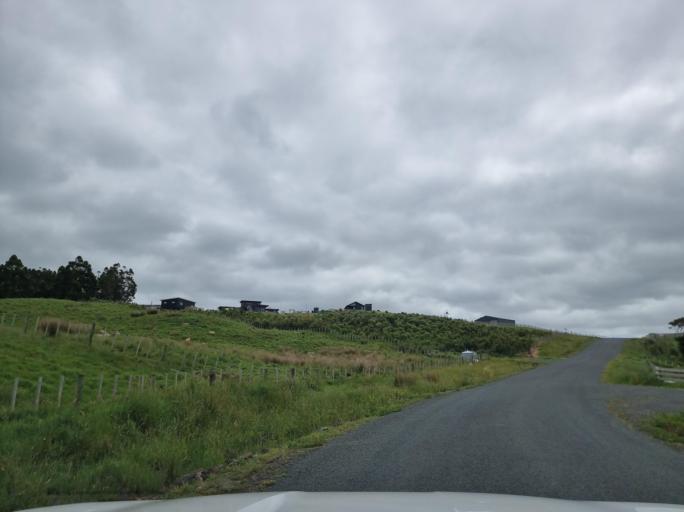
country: NZ
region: Auckland
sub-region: Auckland
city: Wellsford
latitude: -36.1739
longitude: 174.5579
